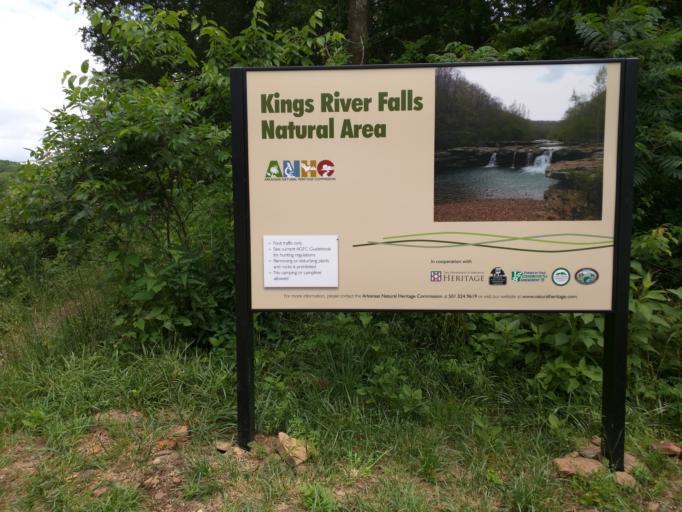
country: US
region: Arkansas
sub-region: Madison County
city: Huntsville
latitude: 35.8946
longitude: -93.5849
